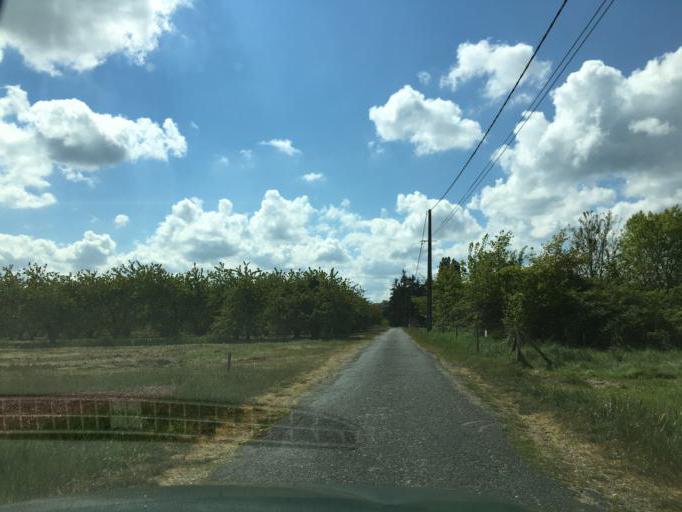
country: FR
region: Centre
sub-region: Departement du Loiret
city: Saint-Pryve-Saint-Mesmin
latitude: 47.8644
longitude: 1.8594
